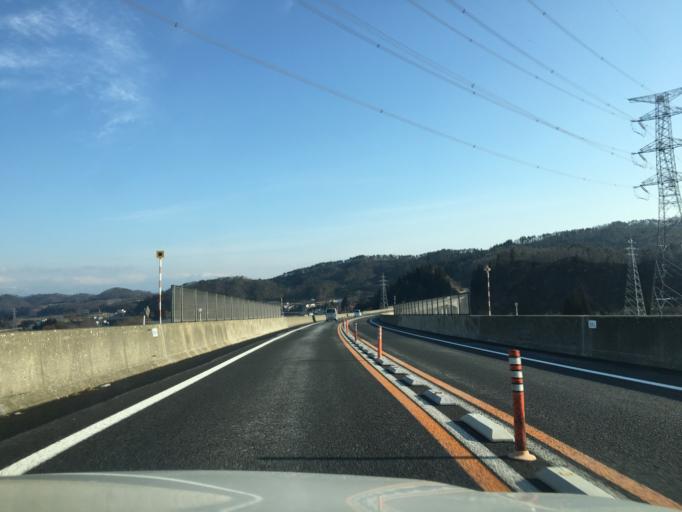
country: JP
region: Yamagata
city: Sagae
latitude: 38.4157
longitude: 140.1889
